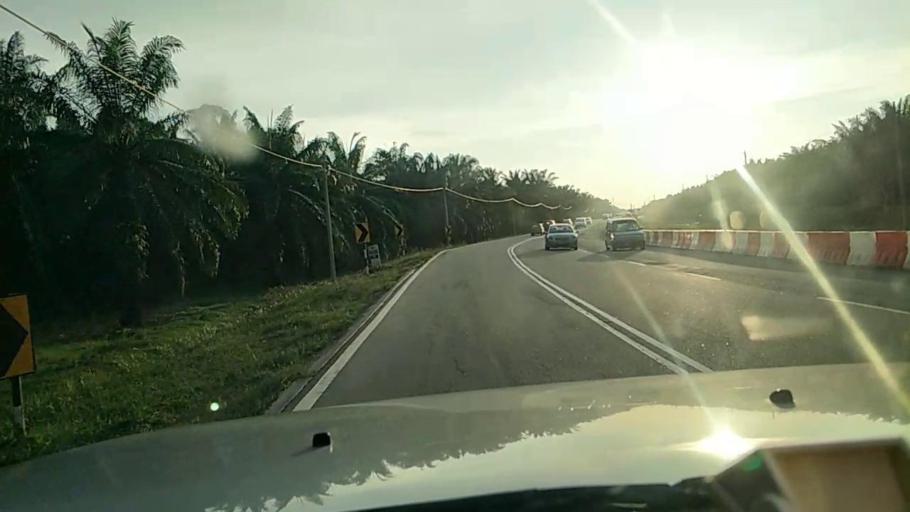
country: MY
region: Perak
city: Kampong Dungun
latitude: 3.3051
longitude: 101.3557
